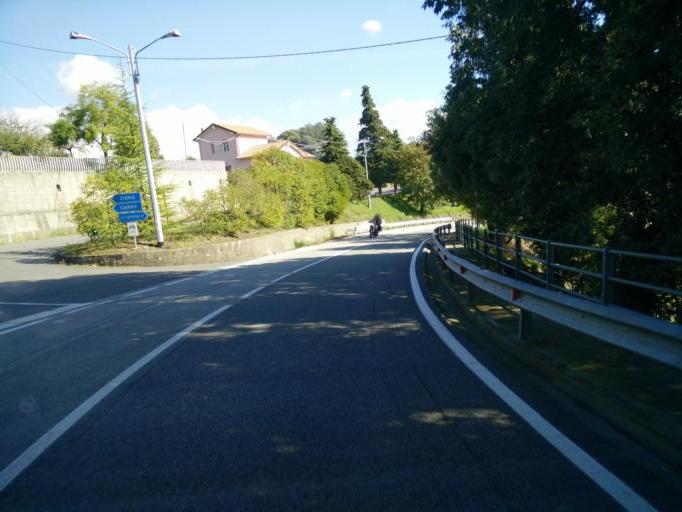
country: IT
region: Liguria
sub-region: Provincia di La Spezia
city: Carrodano
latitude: 44.2468
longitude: 9.6191
